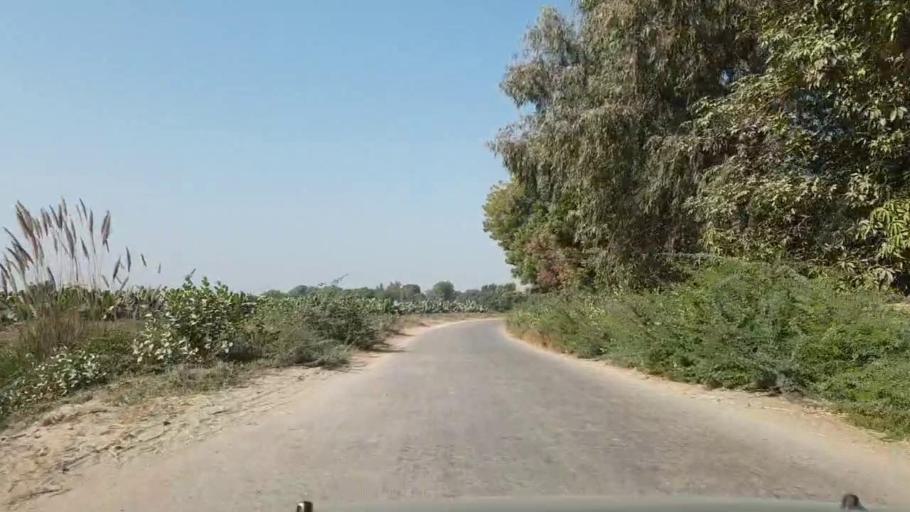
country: PK
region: Sindh
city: Matiari
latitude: 25.6196
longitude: 68.5933
